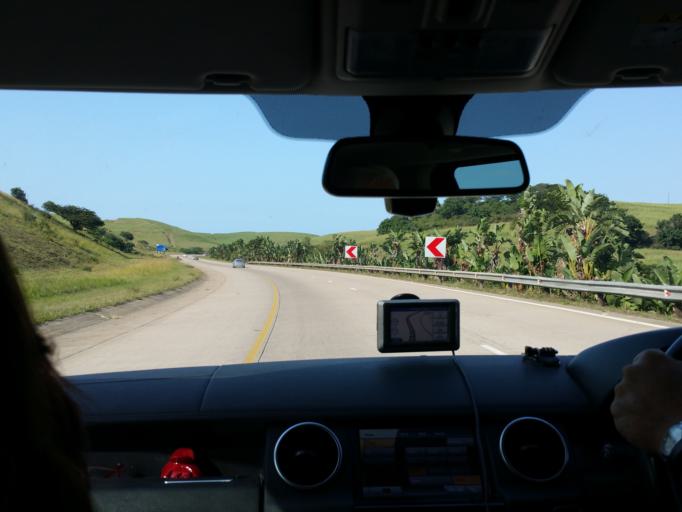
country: ZA
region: KwaZulu-Natal
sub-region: iLembe District Municipality
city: Stanger
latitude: -29.3800
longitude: 31.2956
